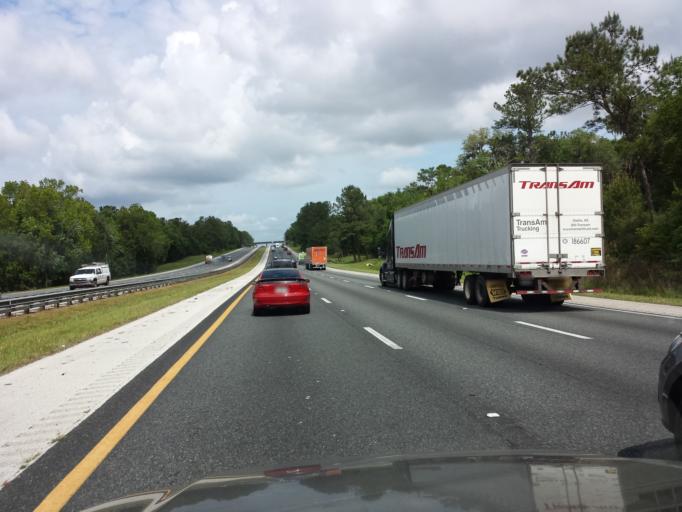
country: US
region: Florida
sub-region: Alachua County
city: Gainesville
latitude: 29.5164
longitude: -82.3050
